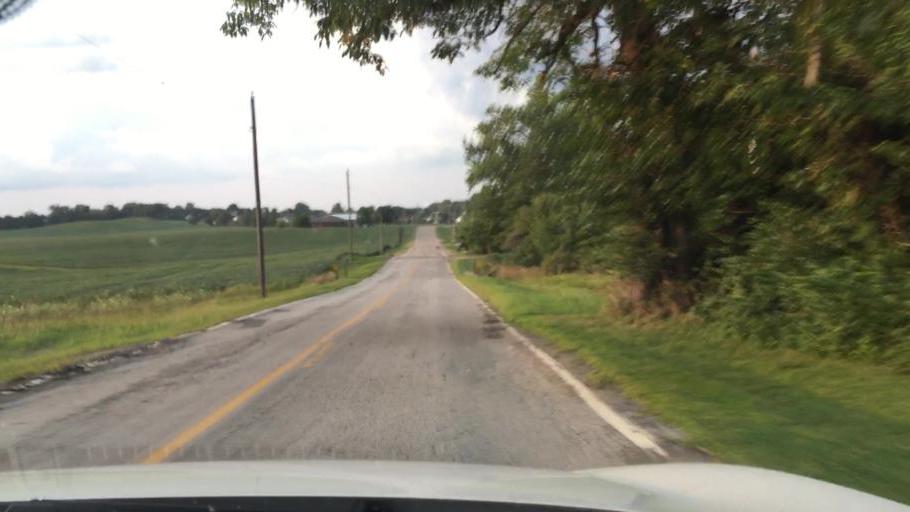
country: US
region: Ohio
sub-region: Champaign County
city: Mechanicsburg
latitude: 40.0133
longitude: -83.5916
